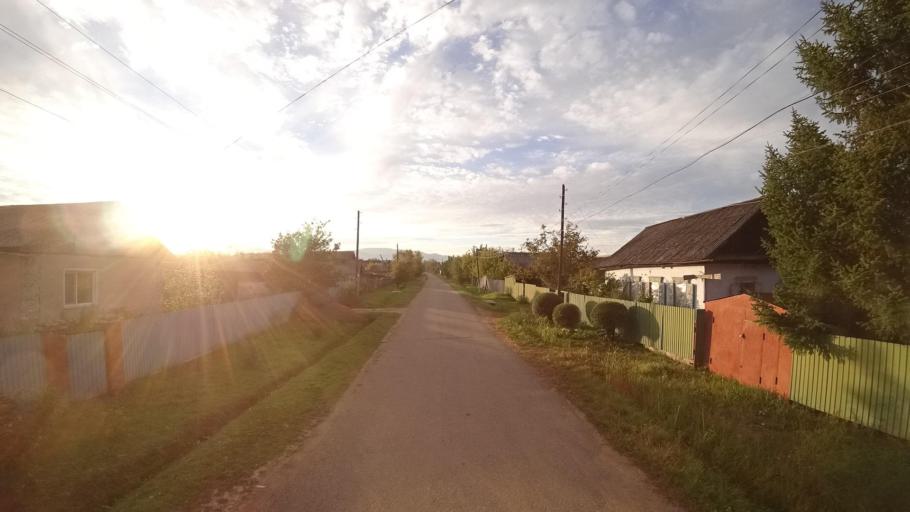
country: RU
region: Primorskiy
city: Yakovlevka
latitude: 44.4239
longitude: 133.4883
